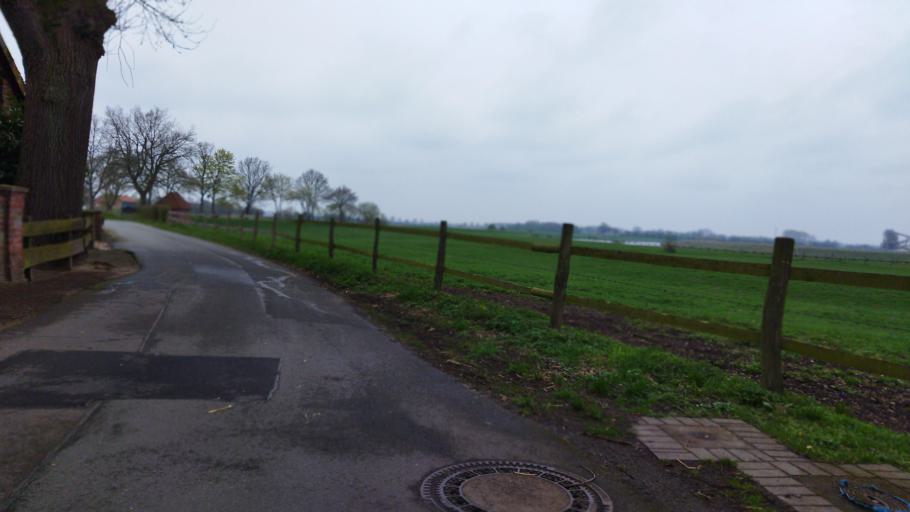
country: DE
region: Lower Saxony
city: Schweringen
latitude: 52.7514
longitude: 9.1815
